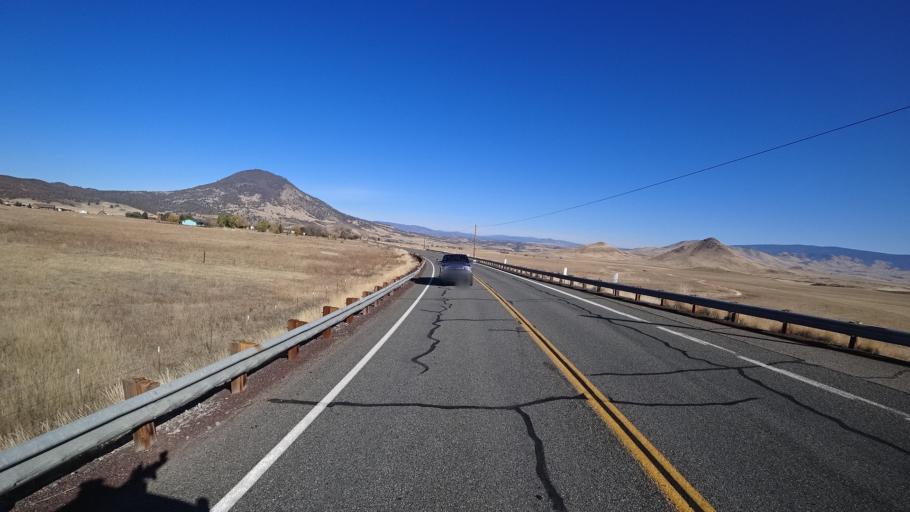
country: US
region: California
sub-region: Siskiyou County
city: Montague
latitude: 41.8076
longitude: -122.4988
